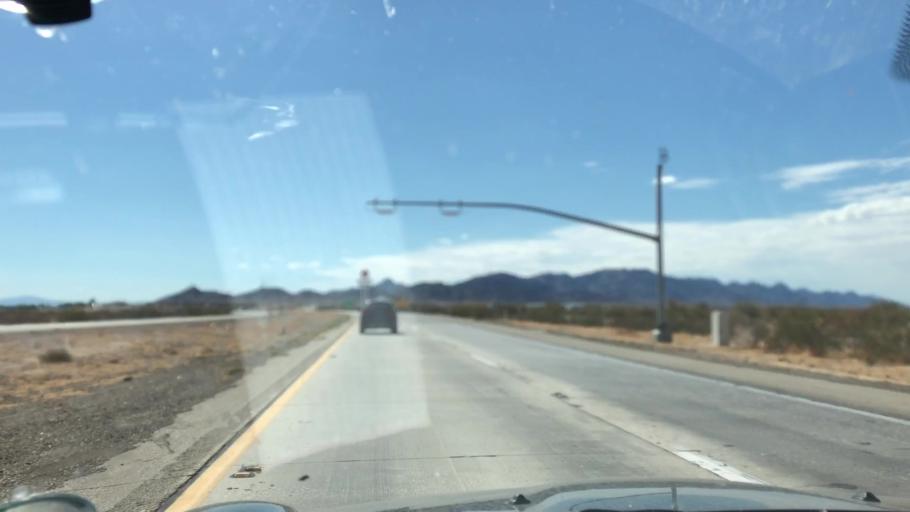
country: US
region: California
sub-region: Riverside County
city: Mesa Verde
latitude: 33.6083
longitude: -114.7184
